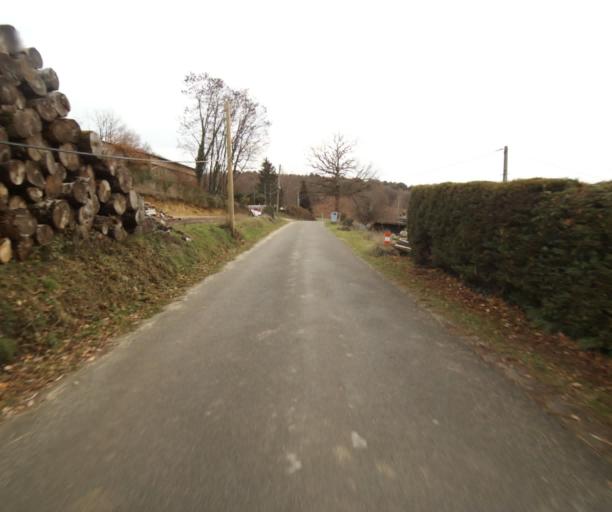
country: FR
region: Limousin
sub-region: Departement de la Correze
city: Chameyrat
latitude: 45.2555
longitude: 1.6757
